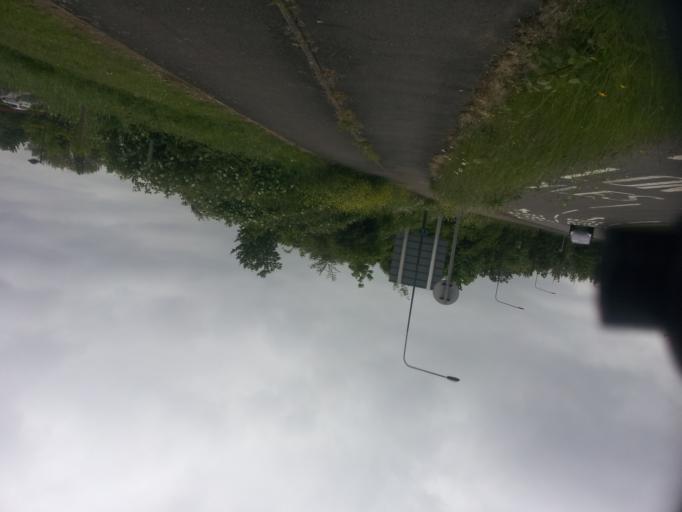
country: GB
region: England
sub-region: Kent
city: Boxley
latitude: 51.2959
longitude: 0.5135
